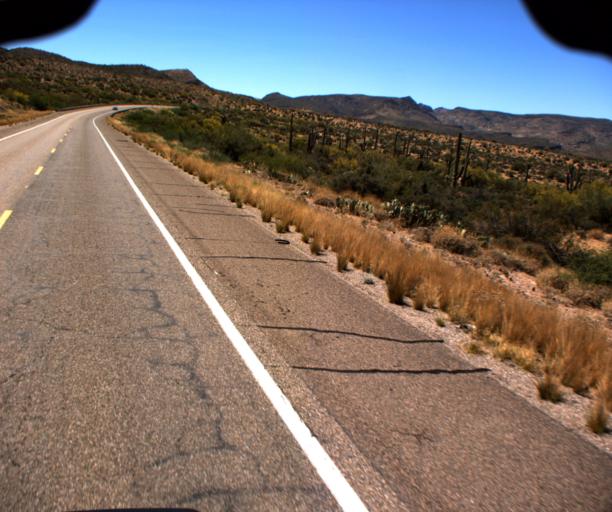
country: US
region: Arizona
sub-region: Pinal County
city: Superior
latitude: 33.2712
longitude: -111.0968
